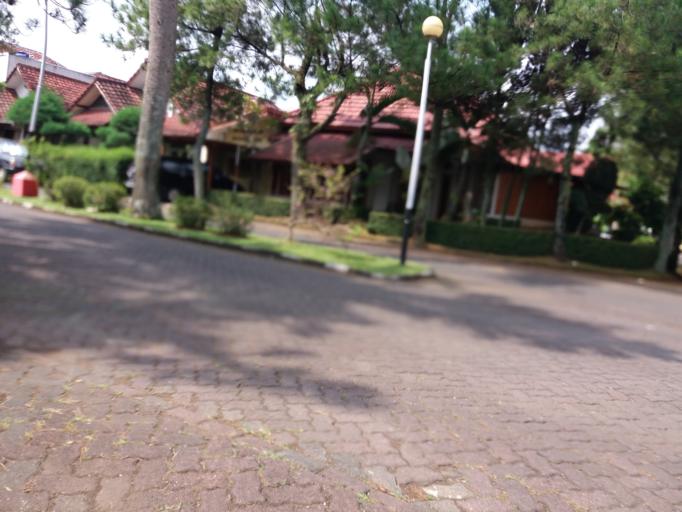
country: ID
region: West Java
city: Bandung
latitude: -6.9171
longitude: 107.6533
